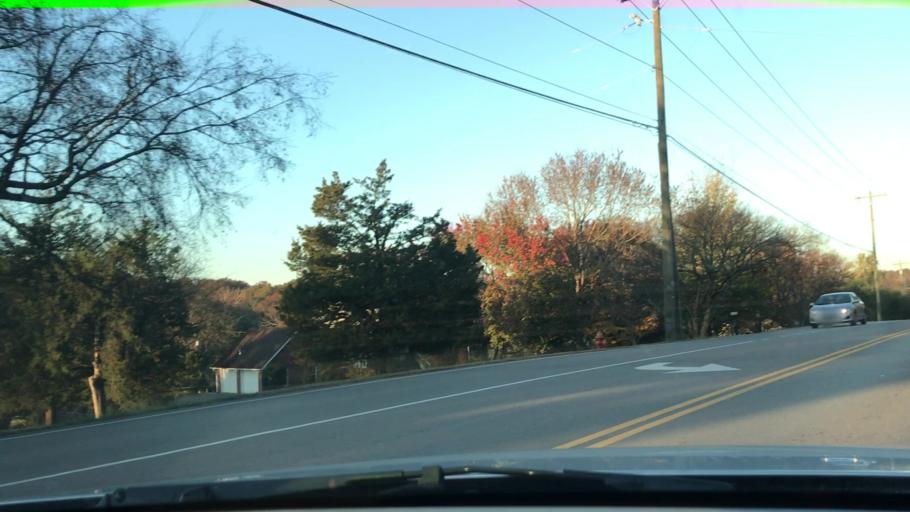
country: US
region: Tennessee
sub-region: Williamson County
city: Brentwood Estates
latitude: 36.0132
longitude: -86.7112
